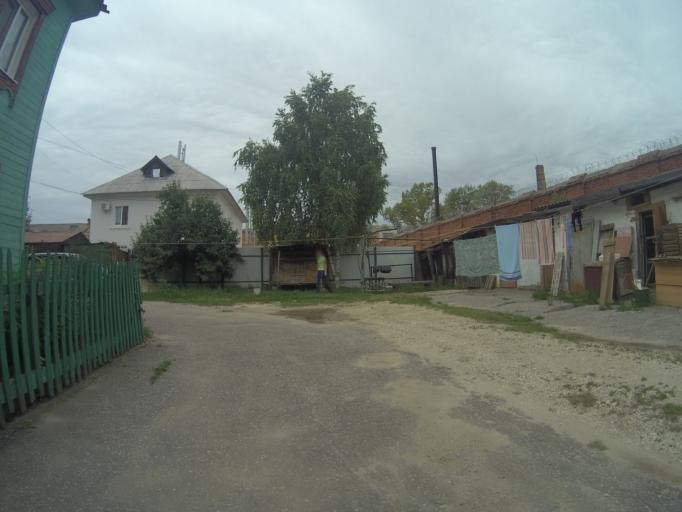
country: RU
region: Vladimir
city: Vladimir
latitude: 56.1259
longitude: 40.3733
